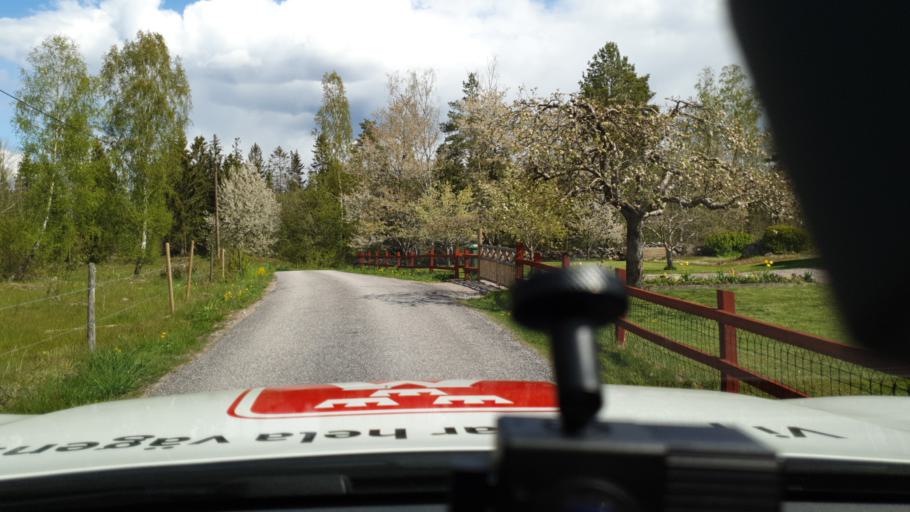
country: SE
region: Kalmar
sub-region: Vasterviks Kommun
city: Ankarsrum
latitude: 57.7816
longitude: 16.1598
